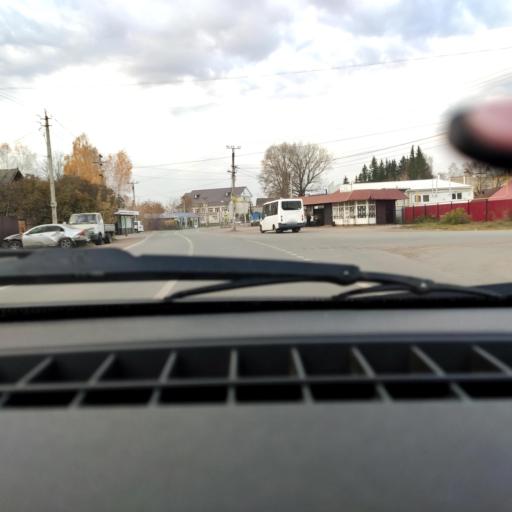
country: RU
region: Bashkortostan
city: Iglino
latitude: 54.8273
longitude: 56.1855
